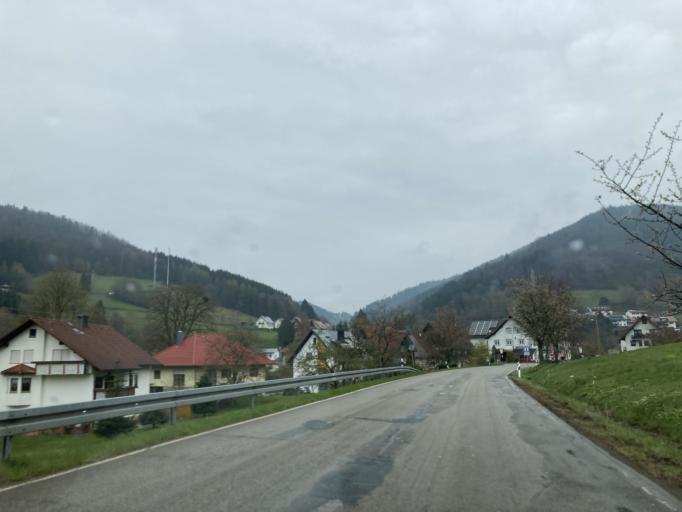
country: DE
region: Baden-Wuerttemberg
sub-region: Freiburg Region
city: Muhlenbach
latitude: 48.2124
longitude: 8.1374
